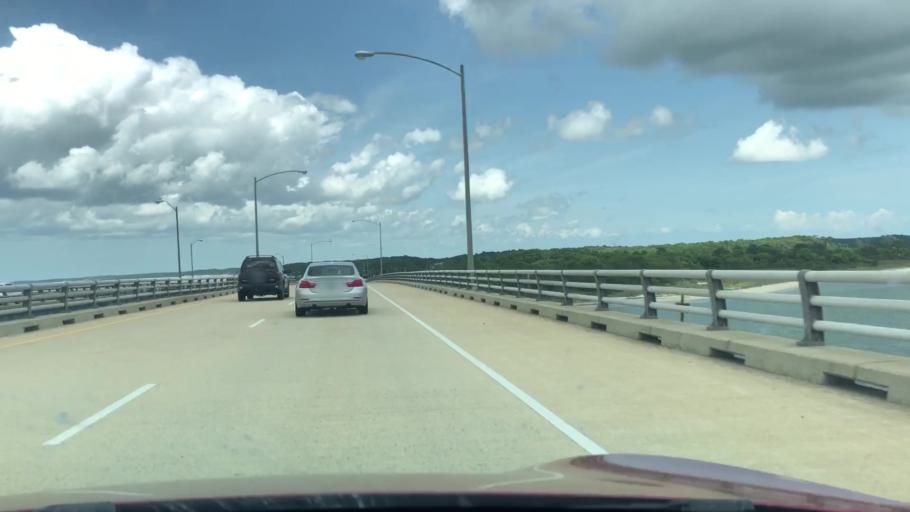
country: US
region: Virginia
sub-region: Northampton County
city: Cape Charles
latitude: 37.1151
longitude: -75.9692
